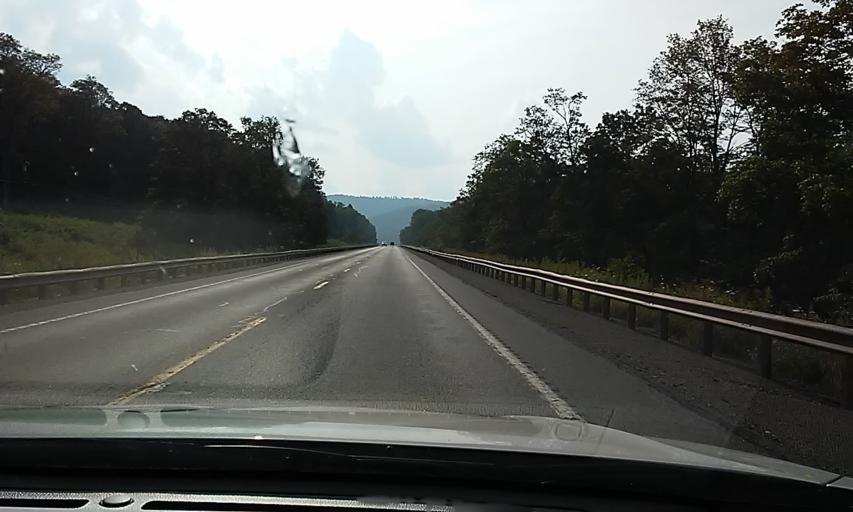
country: US
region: Pennsylvania
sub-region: Potter County
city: Galeton
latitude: 41.7895
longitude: -77.7678
